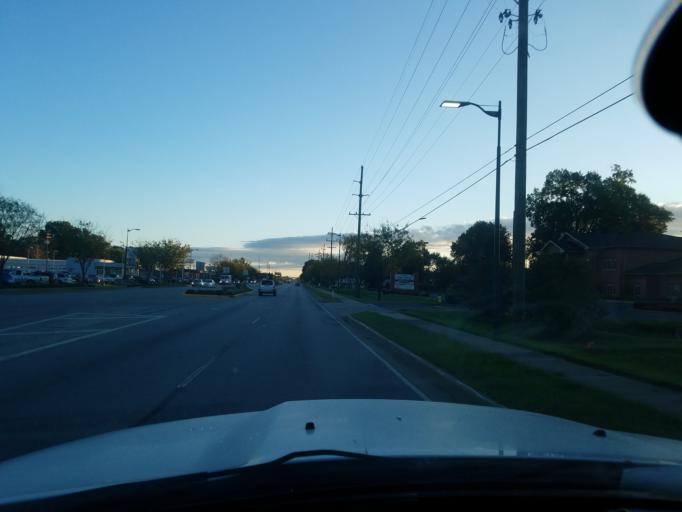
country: US
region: Indiana
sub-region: Clark County
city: Clarksville
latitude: 38.3058
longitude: -85.7767
